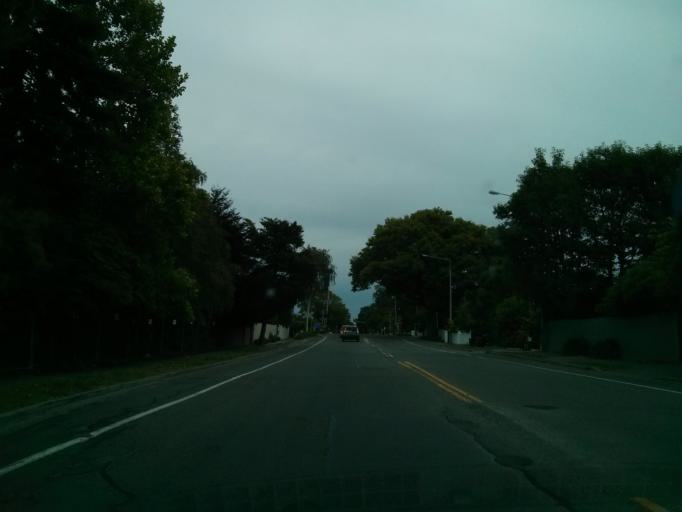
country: NZ
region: Canterbury
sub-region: Christchurch City
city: Christchurch
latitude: -43.5136
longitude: 172.6076
